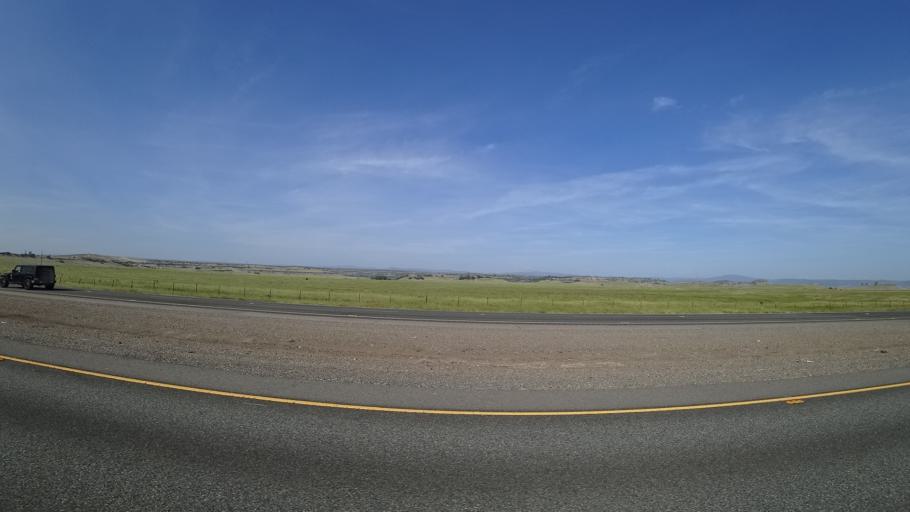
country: US
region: California
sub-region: Butte County
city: Durham
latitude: 39.6505
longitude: -121.7257
